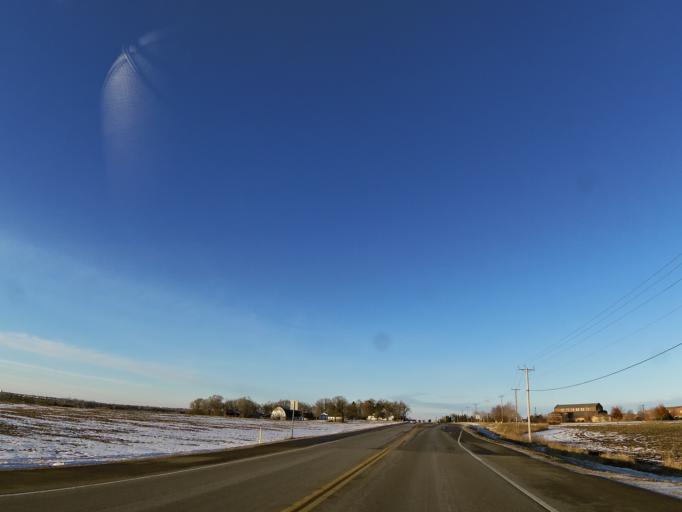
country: US
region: Minnesota
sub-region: Washington County
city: Woodbury
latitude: 44.8853
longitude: -92.9033
